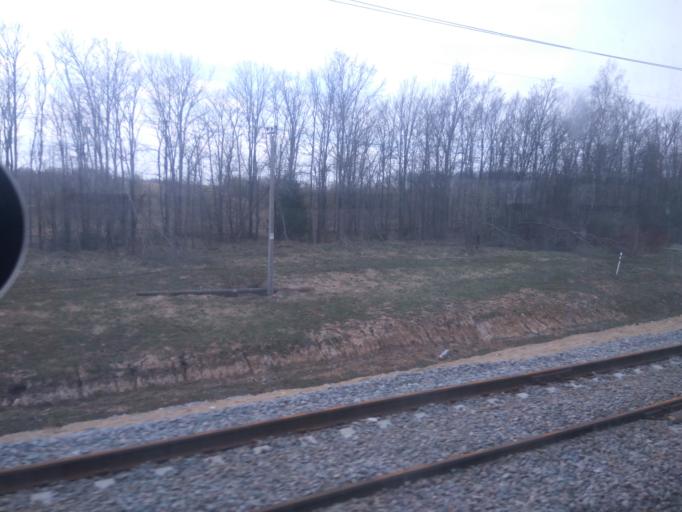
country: RU
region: Moskovskaya
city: Semkhoz
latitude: 56.3352
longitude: 38.0571
